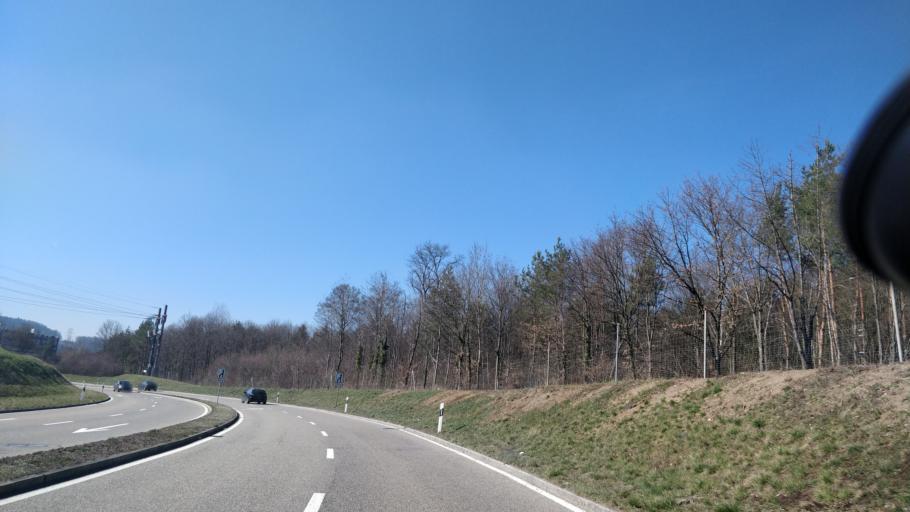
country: CH
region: Zurich
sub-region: Bezirk Buelach
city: Embrach / Kellersacker
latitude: 47.5228
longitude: 8.5936
